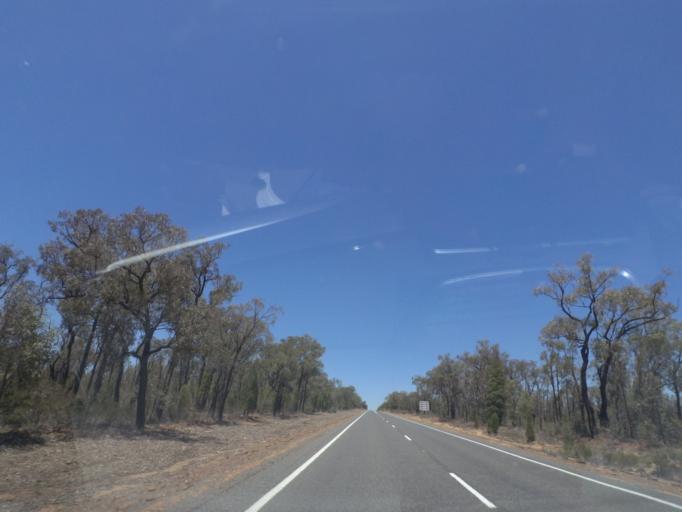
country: AU
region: New South Wales
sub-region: Narrabri
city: Narrabri
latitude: -30.6997
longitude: 149.5351
